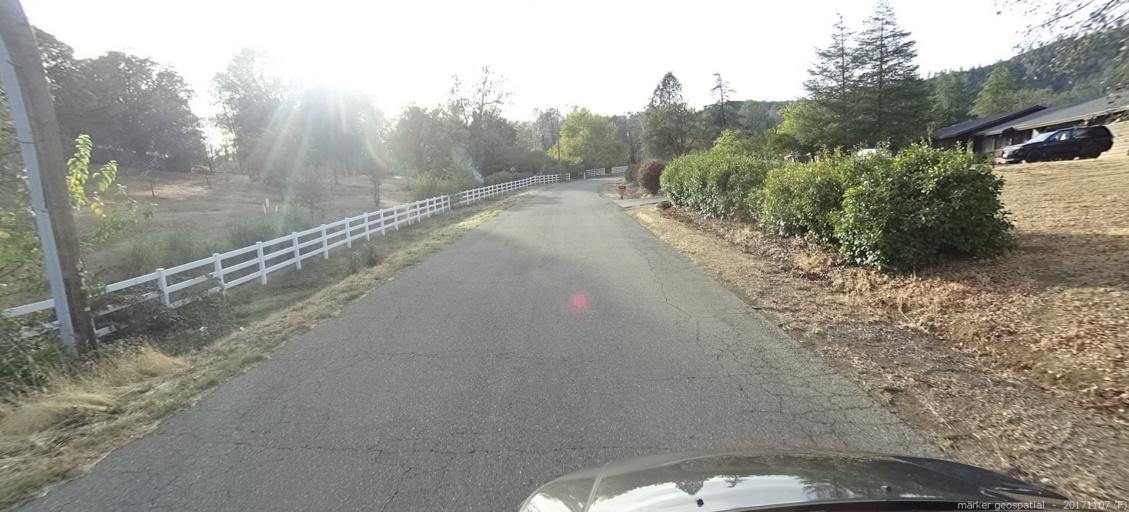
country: US
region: California
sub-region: Shasta County
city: Shasta
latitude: 40.5266
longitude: -122.4801
